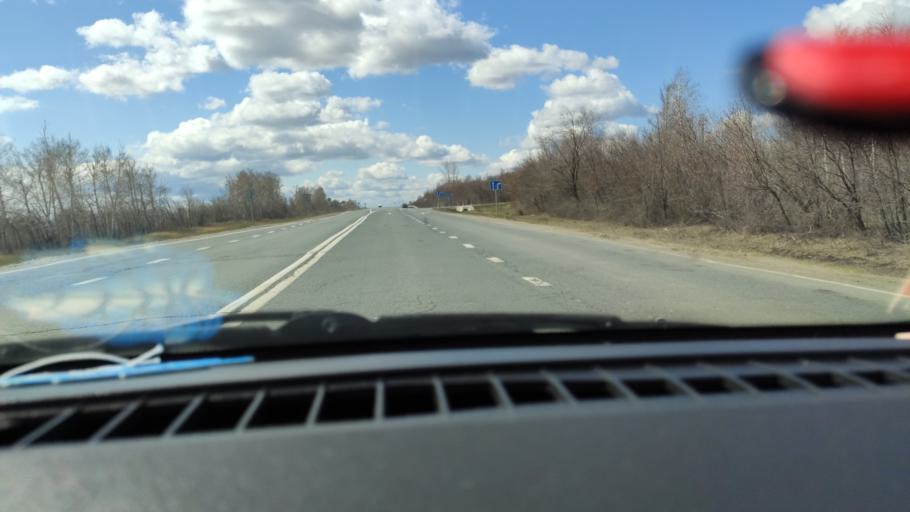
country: RU
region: Saratov
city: Dukhovnitskoye
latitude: 52.6781
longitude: 48.2296
